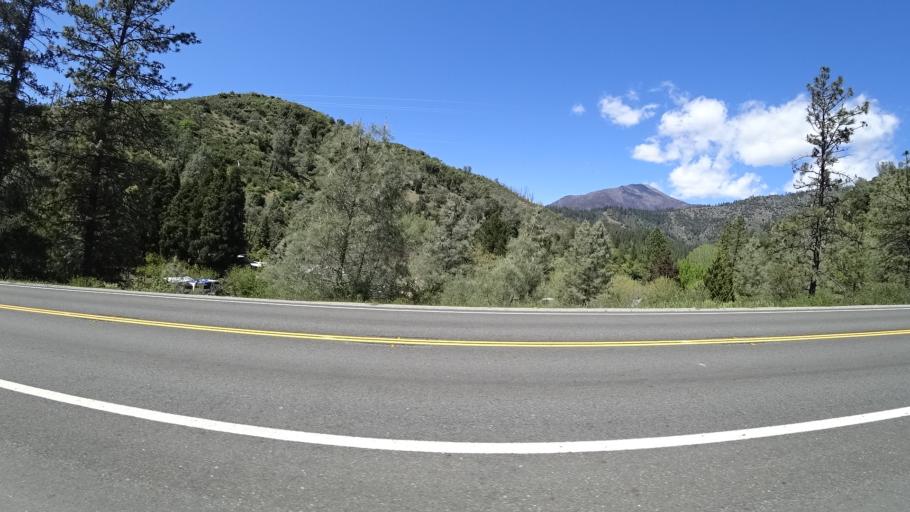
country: US
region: California
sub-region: Trinity County
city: Weaverville
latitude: 40.7328
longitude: -123.0207
